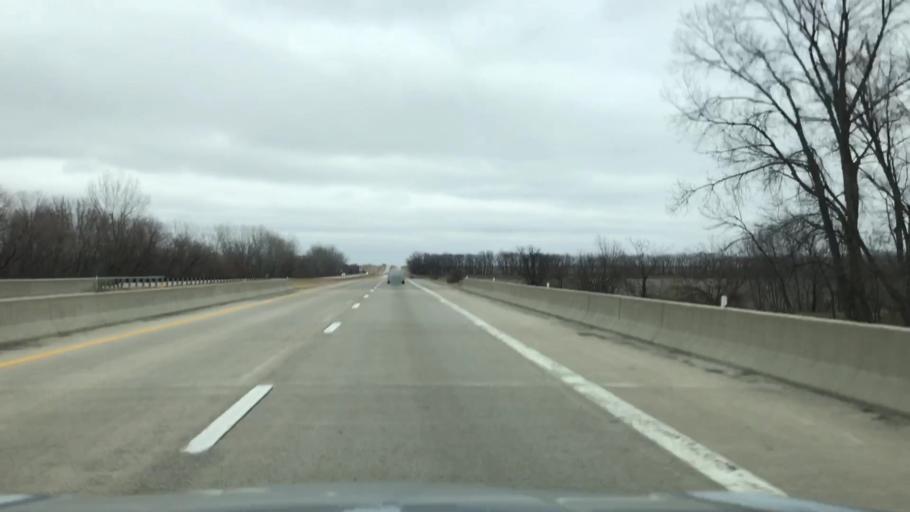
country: US
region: Missouri
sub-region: Livingston County
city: Chillicothe
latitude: 39.7767
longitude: -93.4249
